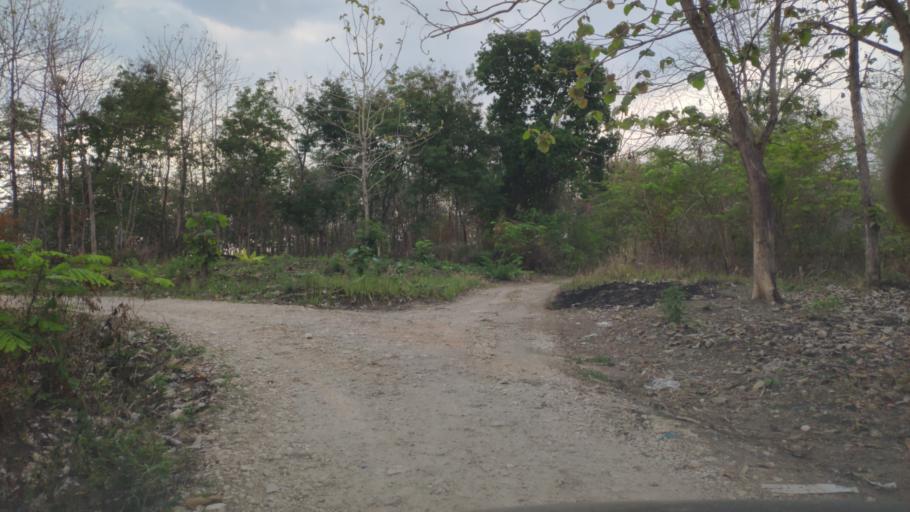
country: ID
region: Central Java
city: Randublatung
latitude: -7.2757
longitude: 111.2855
